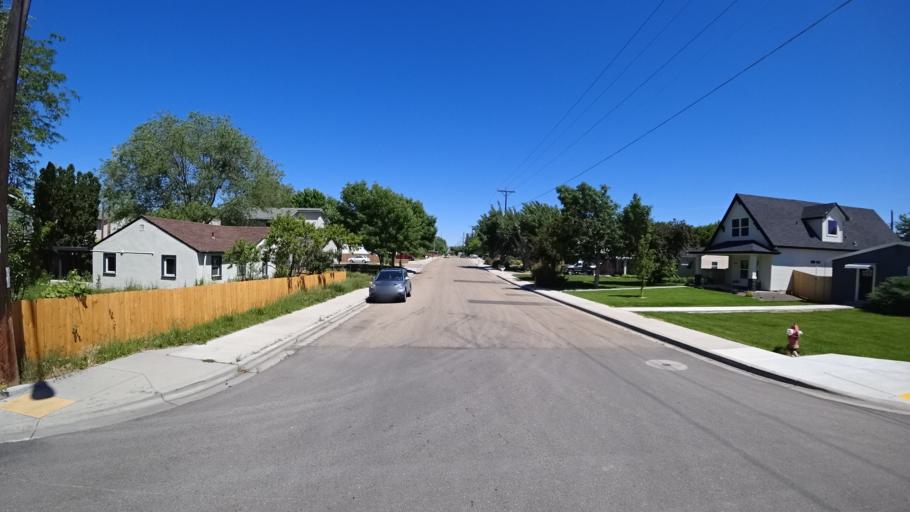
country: US
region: Idaho
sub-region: Ada County
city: Boise
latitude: 43.5851
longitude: -116.2287
